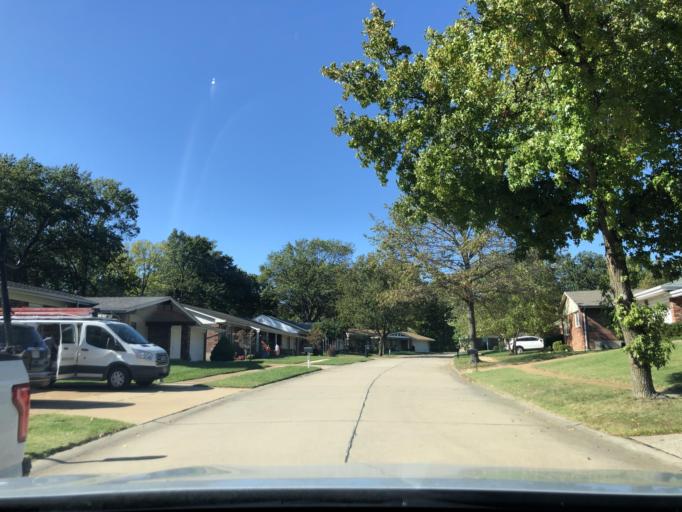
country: US
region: Missouri
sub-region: Saint Louis County
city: Concord
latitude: 38.5032
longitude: -90.3731
